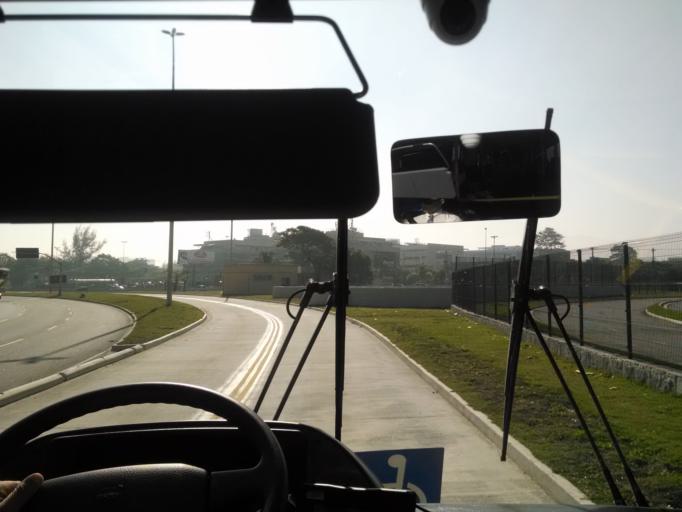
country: BR
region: Rio de Janeiro
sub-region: Rio De Janeiro
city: Rio de Janeiro
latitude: -22.9976
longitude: -43.3663
